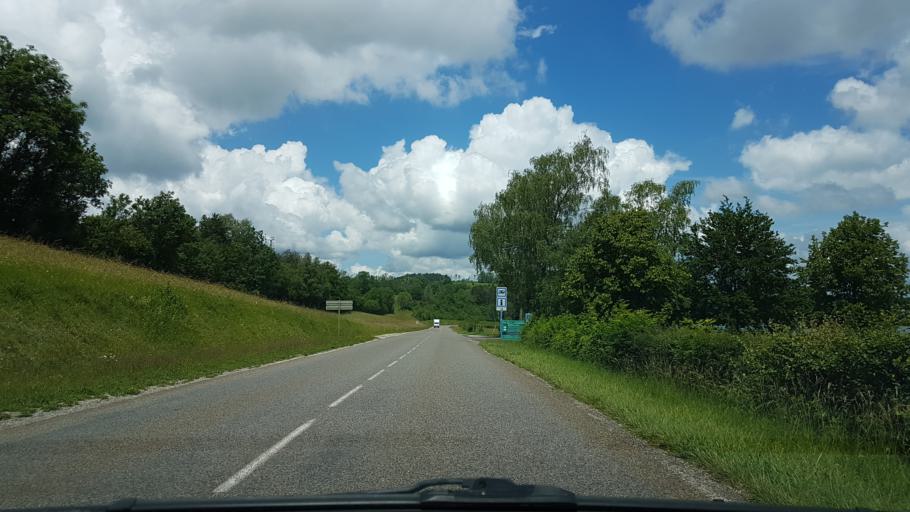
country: FR
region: Franche-Comte
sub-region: Departement du Jura
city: Clairvaux-les-Lacs
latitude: 46.5594
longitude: 5.7448
